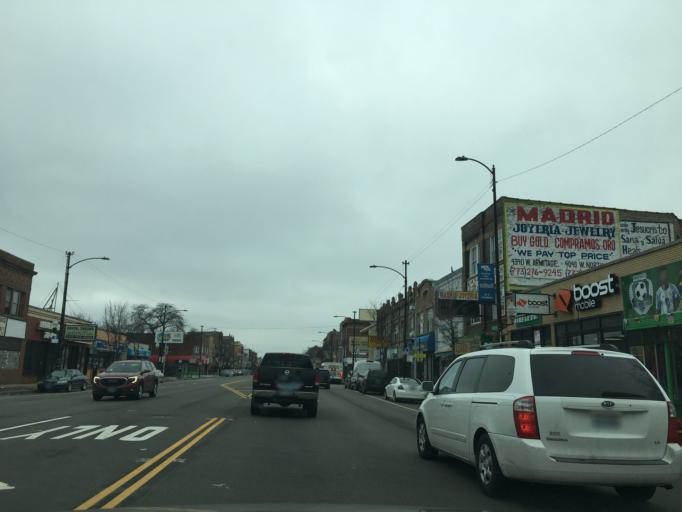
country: US
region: Illinois
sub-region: Cook County
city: Oak Park
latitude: 41.9099
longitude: -87.7275
